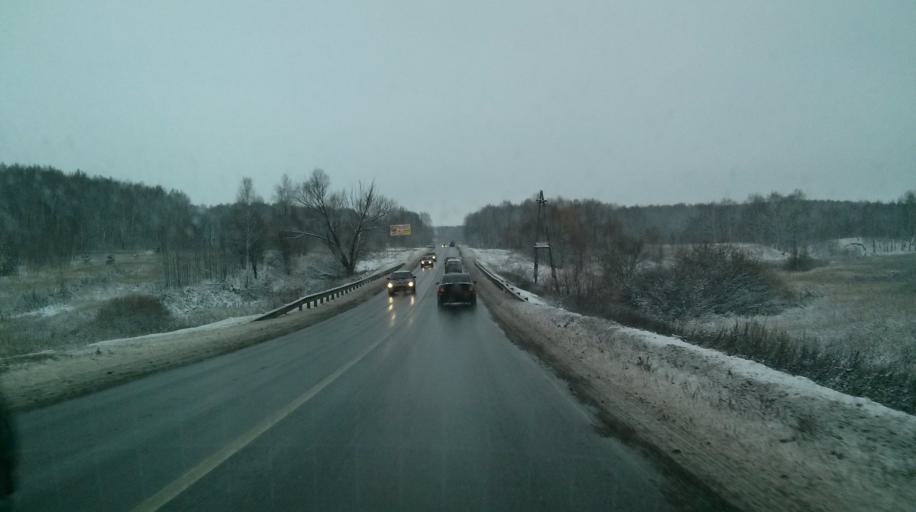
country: RU
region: Nizjnij Novgorod
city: Bogorodsk
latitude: 56.0751
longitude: 43.4607
